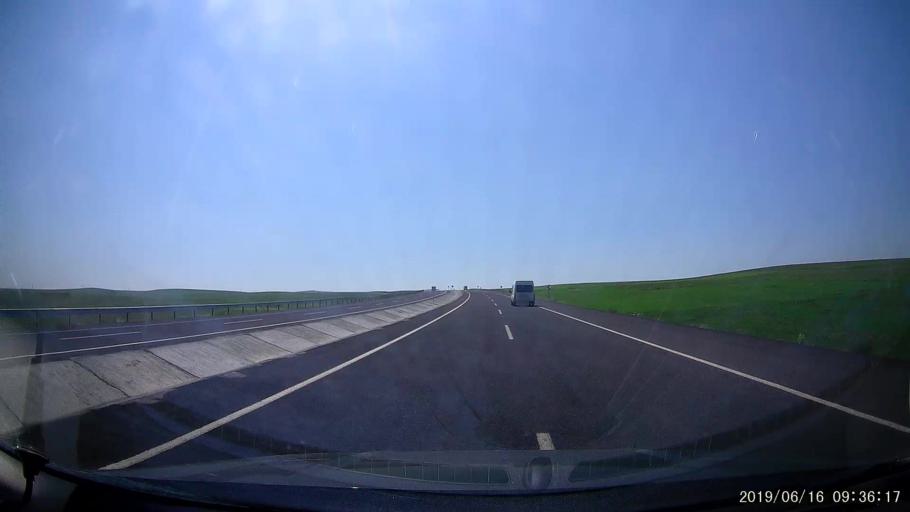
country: TR
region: Kars
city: Kars
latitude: 40.5595
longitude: 43.1695
